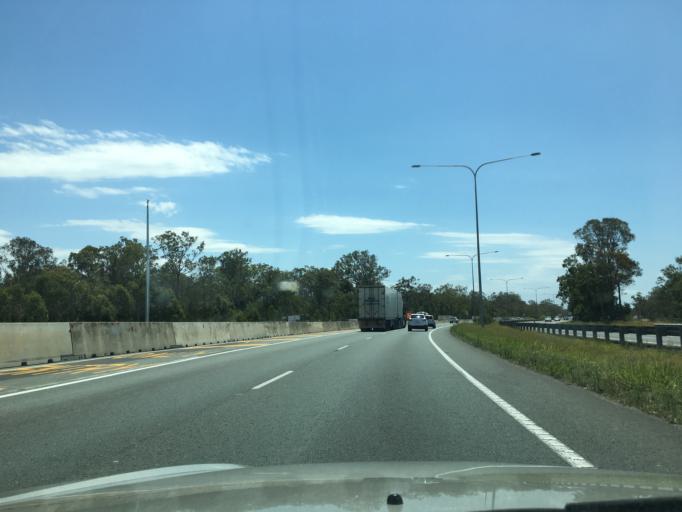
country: AU
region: Queensland
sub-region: Brisbane
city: Deagon
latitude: -27.3532
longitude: 153.0787
